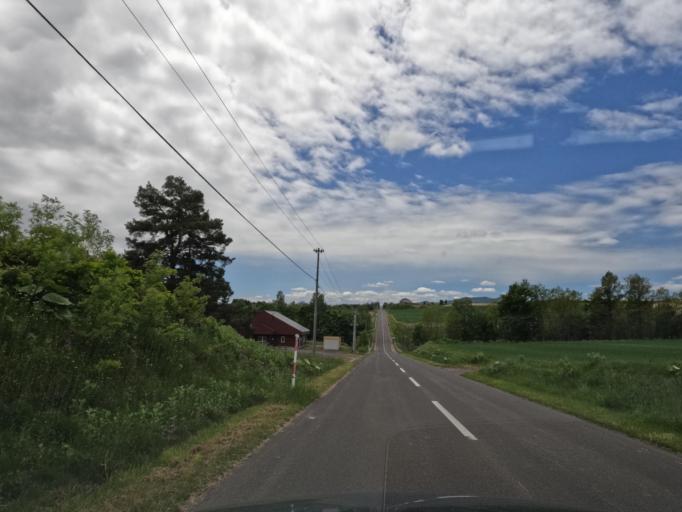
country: JP
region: Hokkaido
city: Shimo-furano
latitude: 43.5302
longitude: 142.4390
